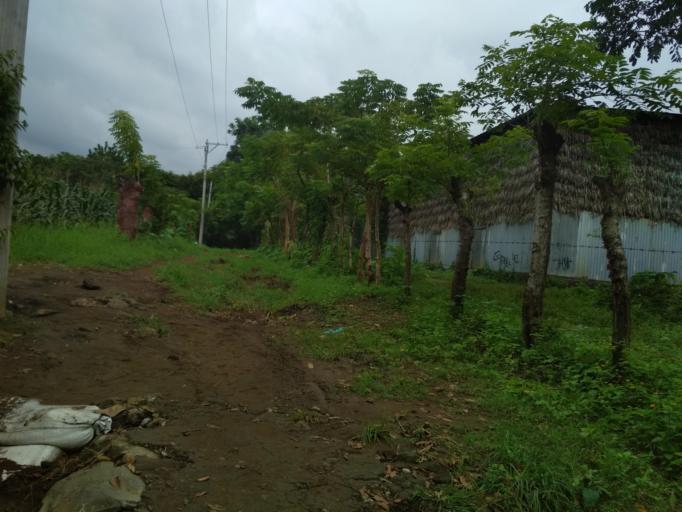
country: MX
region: Veracruz
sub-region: San Andres Tuxtla
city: Matacapan
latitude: 18.4372
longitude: -95.1657
